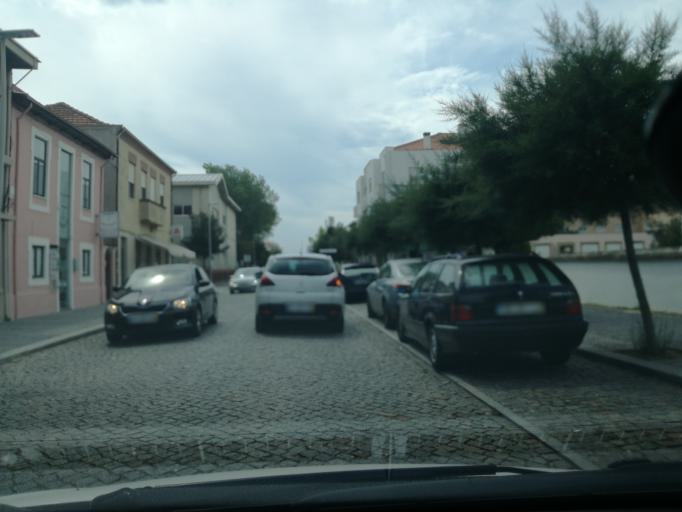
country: PT
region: Aveiro
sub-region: Espinho
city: Espinho
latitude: 41.0057
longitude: -8.6399
